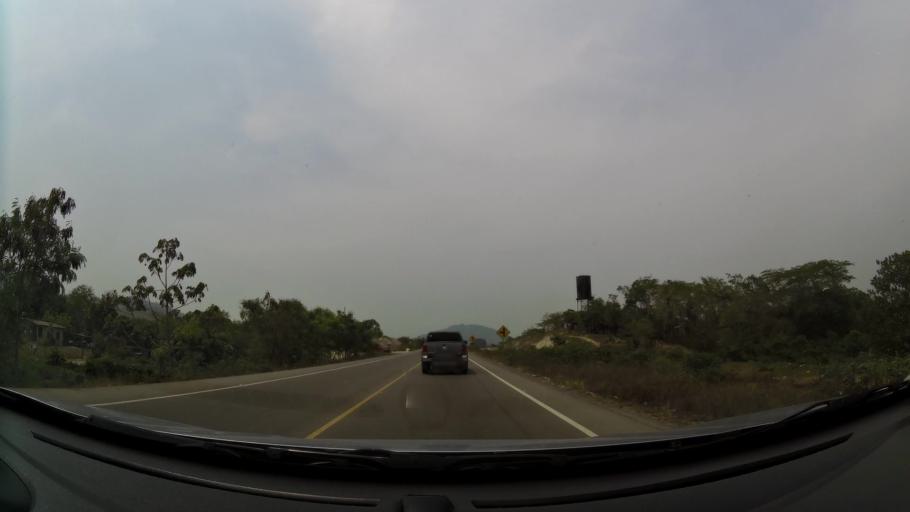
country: HN
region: Cortes
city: Potrerillos
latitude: 15.2350
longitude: -87.9585
